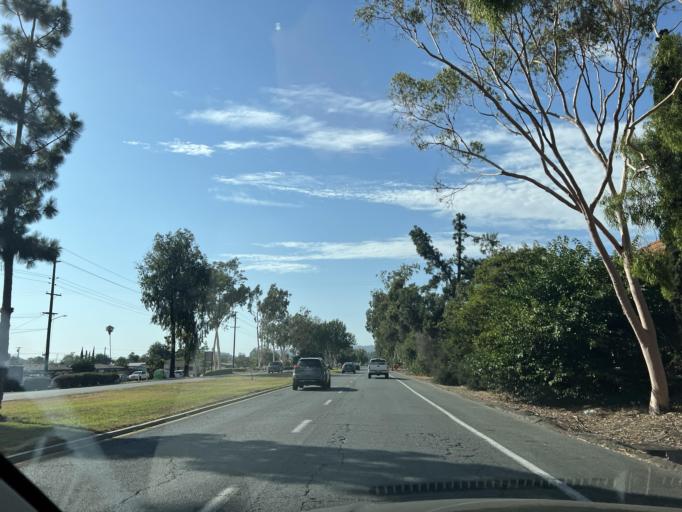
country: US
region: California
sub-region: San Diego County
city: Escondido
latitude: 33.1128
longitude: -117.0821
